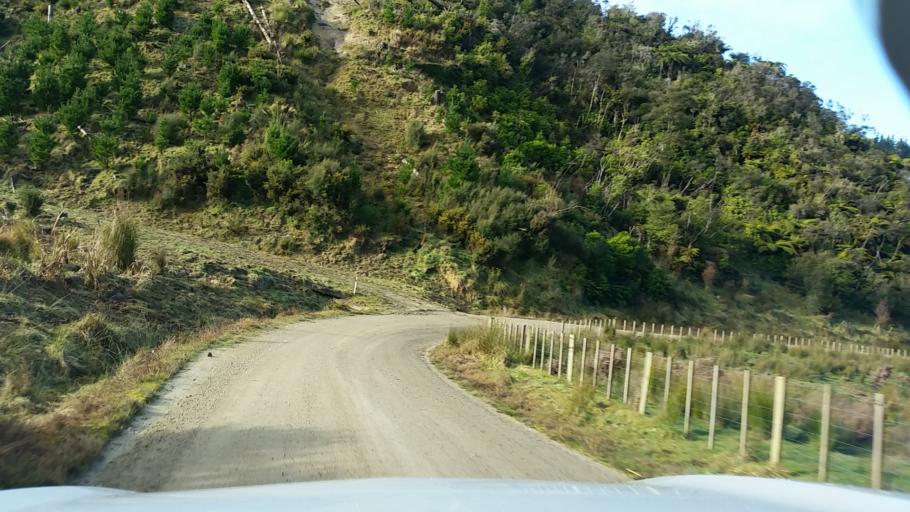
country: NZ
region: Taranaki
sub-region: South Taranaki District
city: Patea
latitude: -39.6771
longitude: 174.7650
